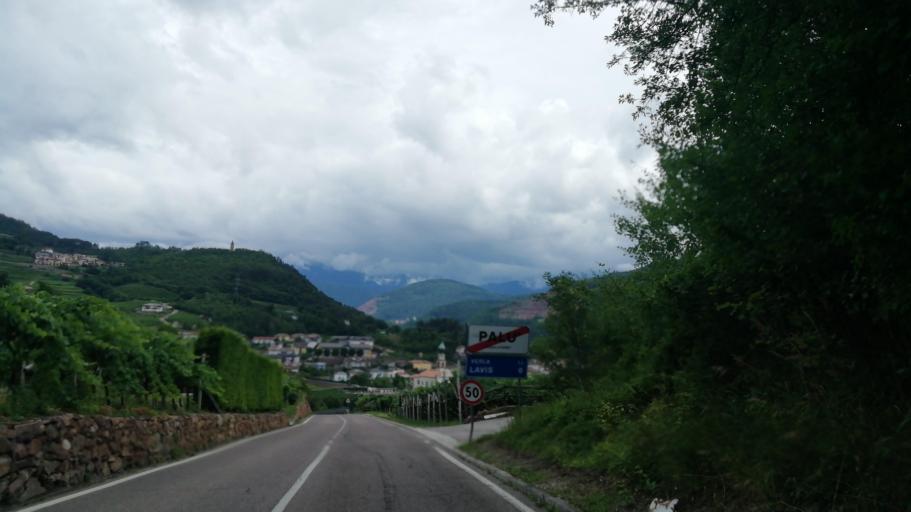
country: IT
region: Trentino-Alto Adige
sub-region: Provincia di Trento
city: Verla
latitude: 46.1596
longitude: 11.1450
